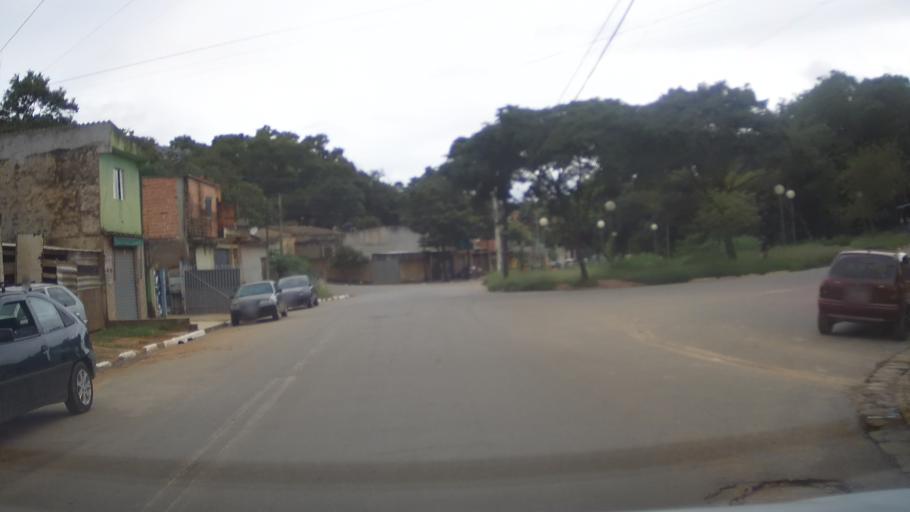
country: BR
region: Sao Paulo
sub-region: Aruja
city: Aruja
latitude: -23.3852
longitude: -46.3988
